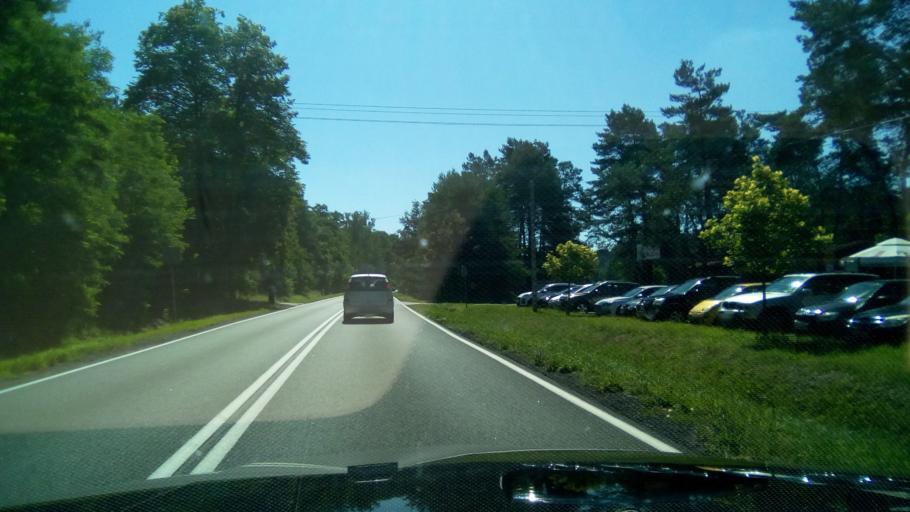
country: PL
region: Lodz Voivodeship
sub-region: Powiat tomaszowski
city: Inowlodz
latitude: 51.5250
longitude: 20.1946
